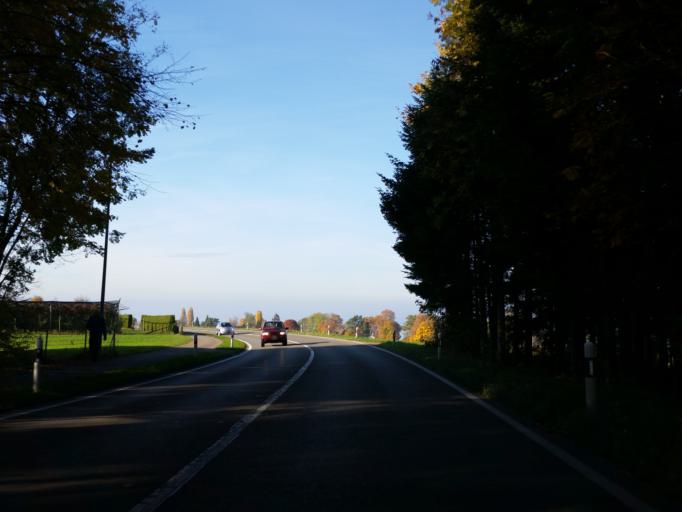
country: CH
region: Thurgau
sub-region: Arbon District
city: Uttwil
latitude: 47.5785
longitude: 9.3542
